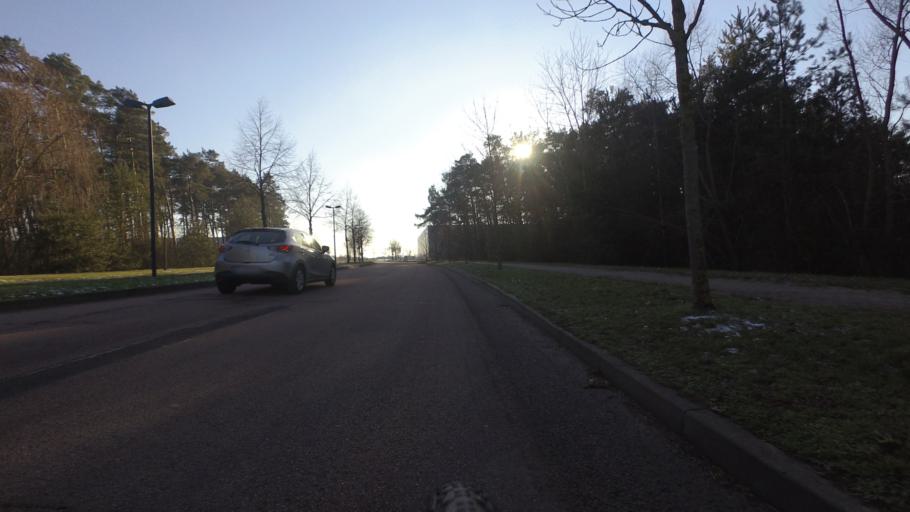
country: DE
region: Brandenburg
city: Ludwigsfelde
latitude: 52.3178
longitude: 13.2921
